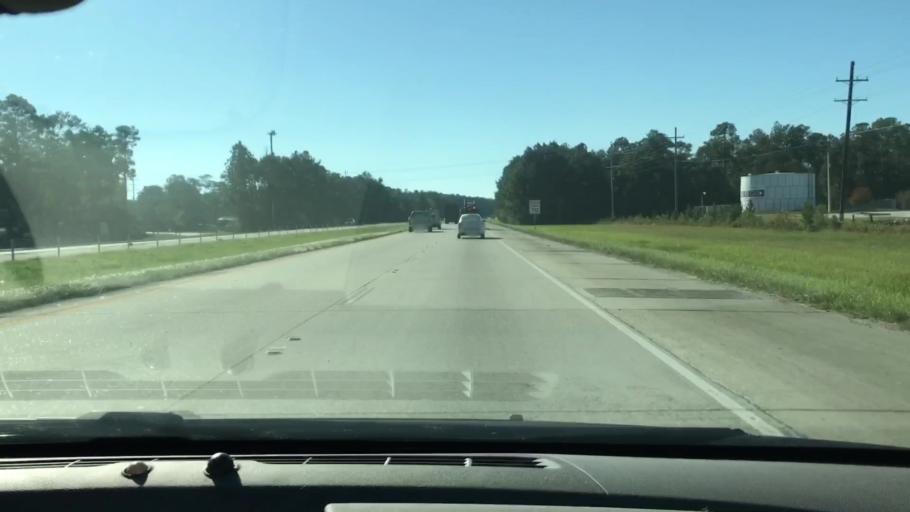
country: US
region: Louisiana
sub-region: Saint Tammany Parish
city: Pearl River
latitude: 30.3453
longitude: -89.7392
